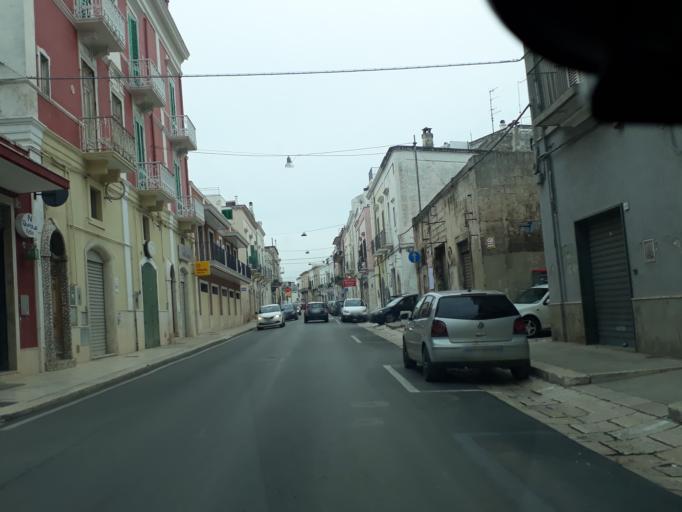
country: IT
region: Apulia
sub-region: Provincia di Brindisi
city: Fasano
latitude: 40.8383
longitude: 17.3601
